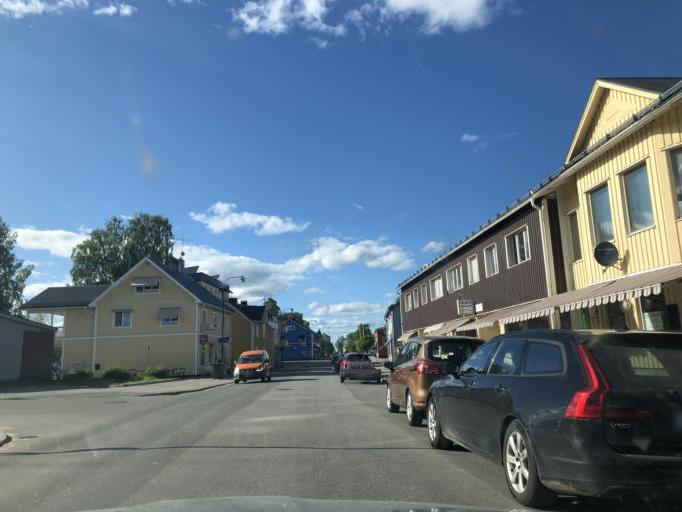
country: SE
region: Norrbotten
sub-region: Overkalix Kommun
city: OEverkalix
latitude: 66.3254
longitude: 22.8458
